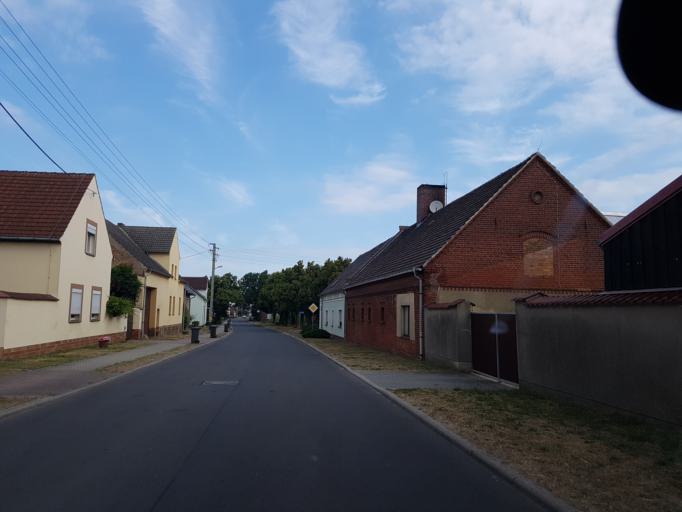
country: DE
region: Brandenburg
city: Luckau
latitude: 51.8351
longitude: 13.6421
